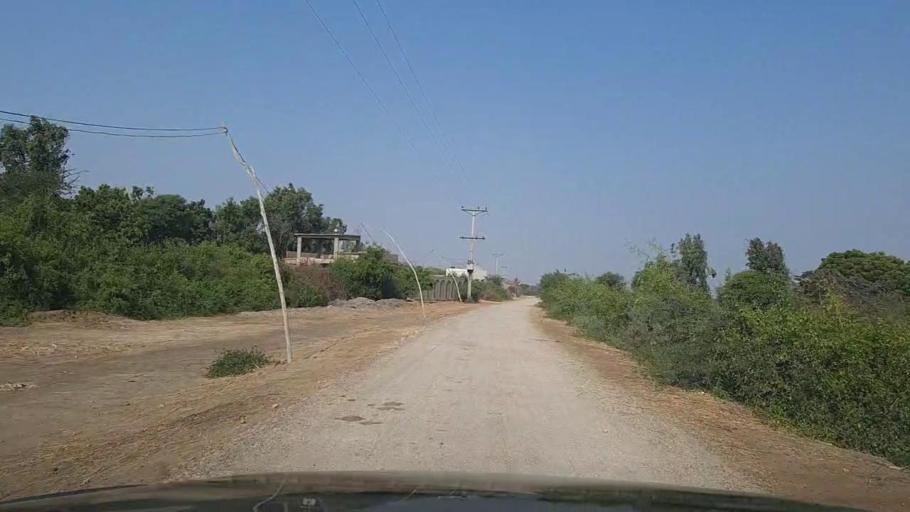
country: PK
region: Sindh
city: Thatta
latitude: 24.6149
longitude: 67.8196
